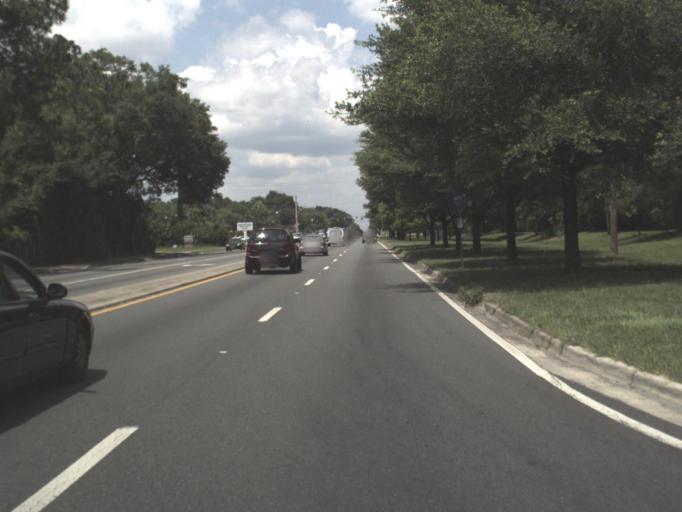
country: US
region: Florida
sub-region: Alachua County
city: Gainesville
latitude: 29.6638
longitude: -82.3035
